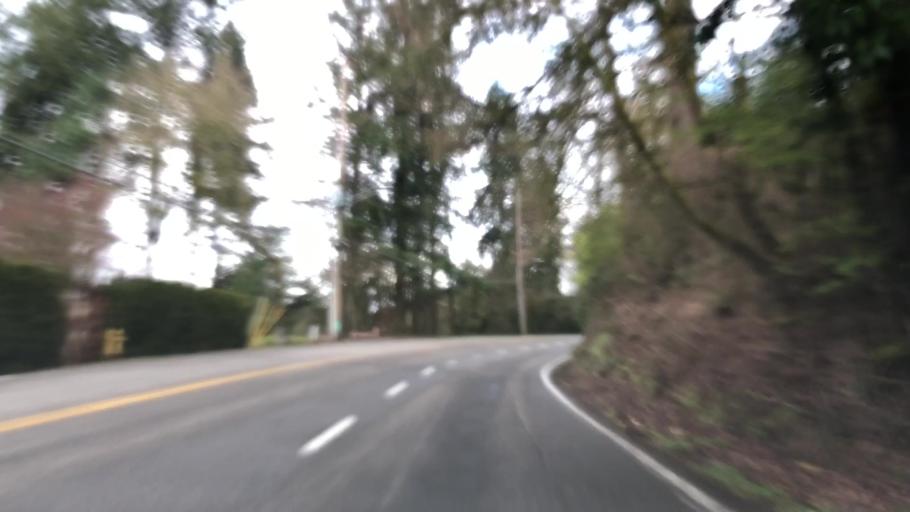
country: US
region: Oregon
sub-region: Washington County
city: West Slope
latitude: 45.4995
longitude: -122.7403
